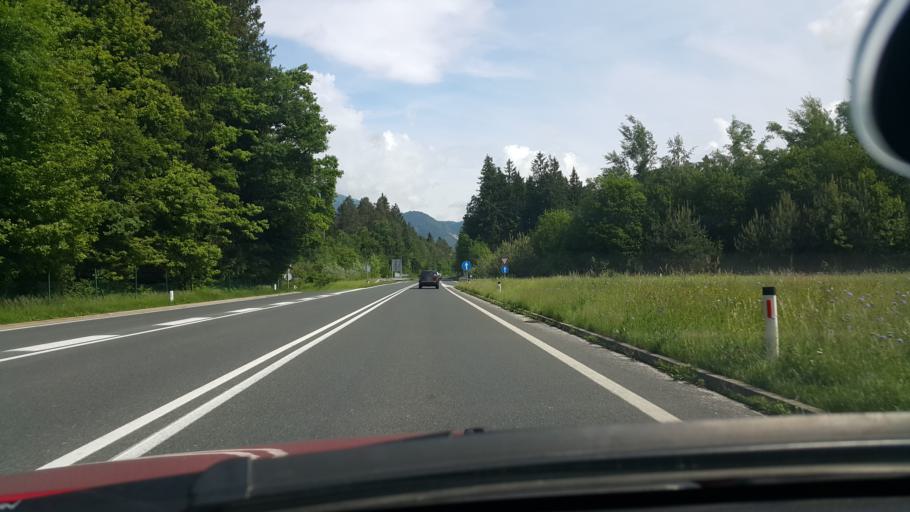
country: SI
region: Trzic
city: Bistrica pri Trzicu
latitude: 46.3150
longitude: 14.2785
